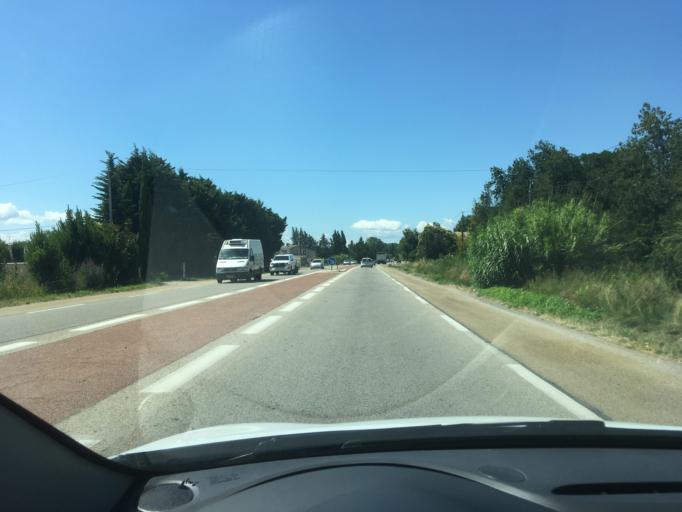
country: FR
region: Provence-Alpes-Cote d'Azur
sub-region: Departement des Bouches-du-Rhone
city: Chateaurenard
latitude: 43.8893
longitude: 4.8363
